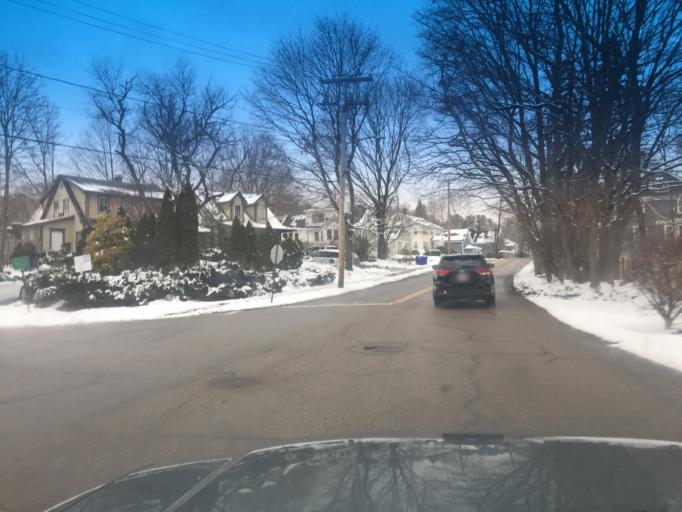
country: US
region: Massachusetts
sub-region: Norfolk County
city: Millis
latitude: 42.1722
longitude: -71.3563
